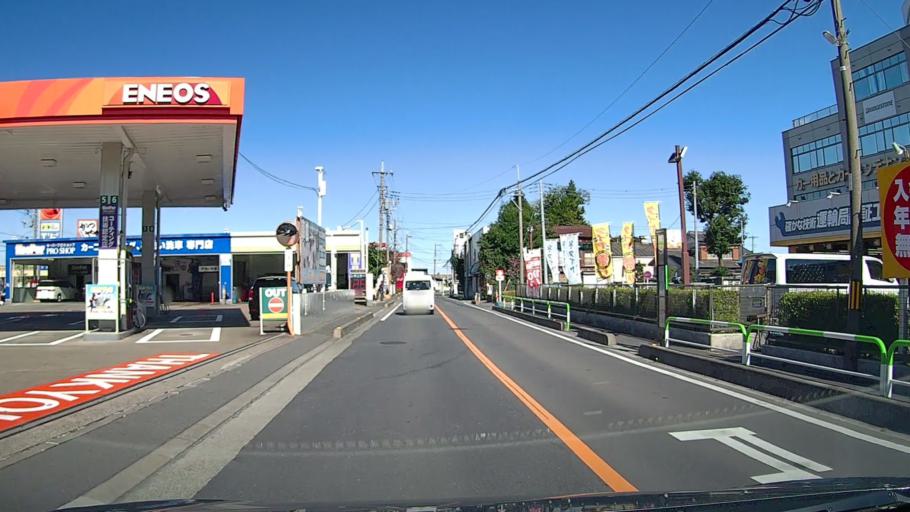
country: JP
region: Saitama
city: Wako
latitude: 35.7677
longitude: 139.6202
